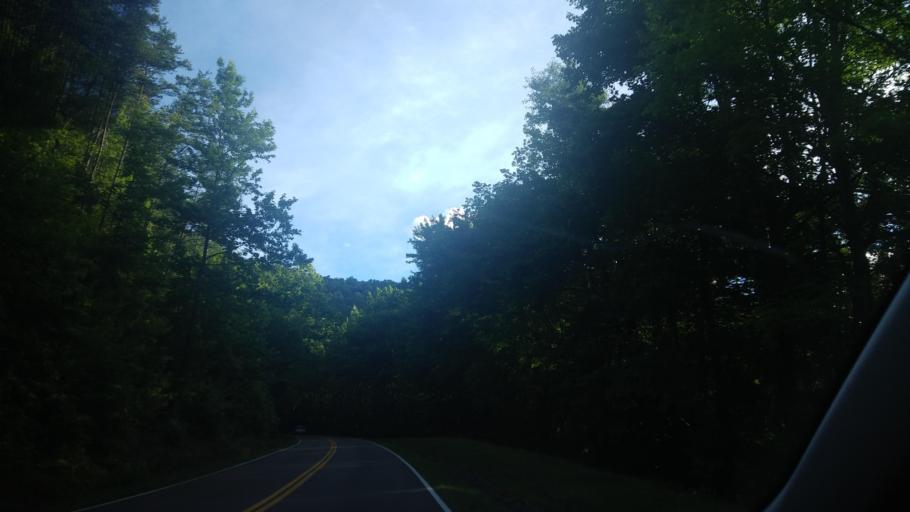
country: US
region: Tennessee
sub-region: Cocke County
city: Newport
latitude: 35.8054
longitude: -83.2383
